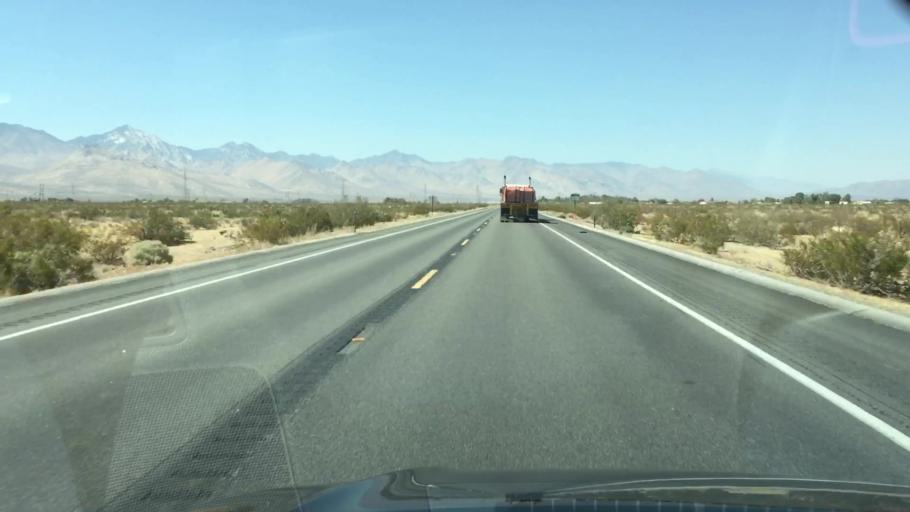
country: US
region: California
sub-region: Kern County
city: China Lake Acres
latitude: 35.6257
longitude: -117.7783
